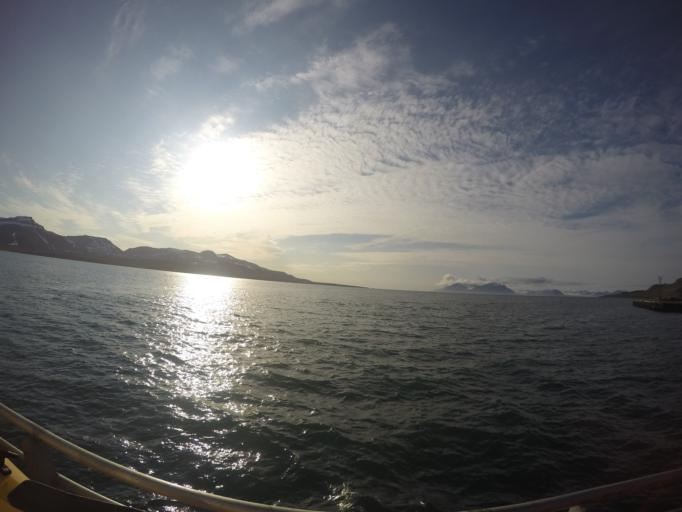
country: SJ
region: Svalbard
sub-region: Spitsbergen
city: Longyearbyen
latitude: 78.0626
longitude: 14.2010
